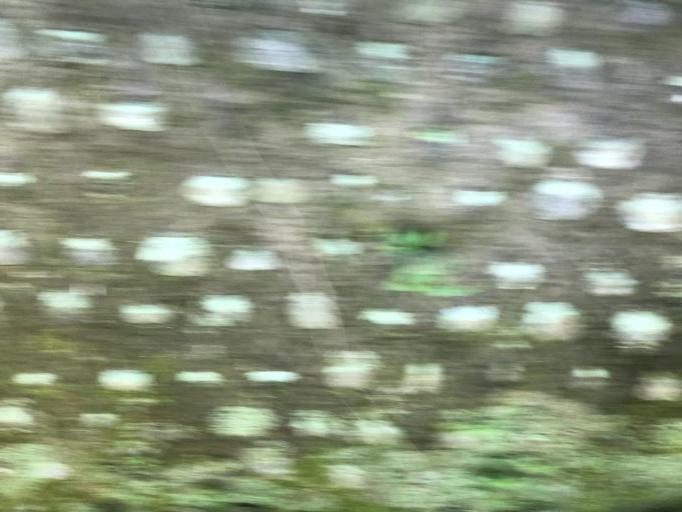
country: TW
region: Taiwan
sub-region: Keelung
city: Keelung
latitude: 25.1931
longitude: 121.6439
